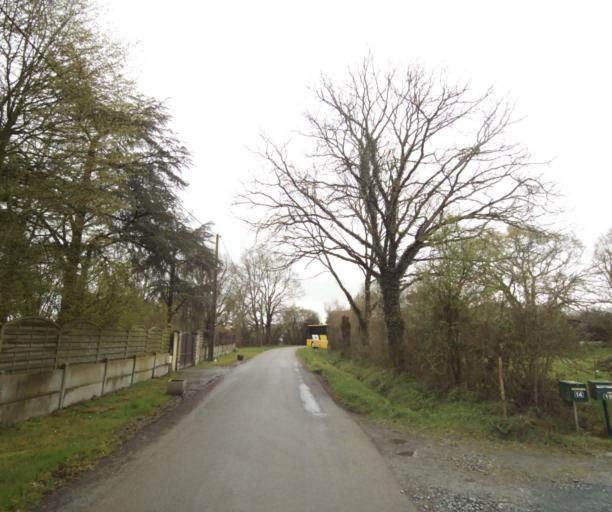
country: FR
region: Pays de la Loire
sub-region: Departement de la Loire-Atlantique
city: Bouvron
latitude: 47.4401
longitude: -1.8827
